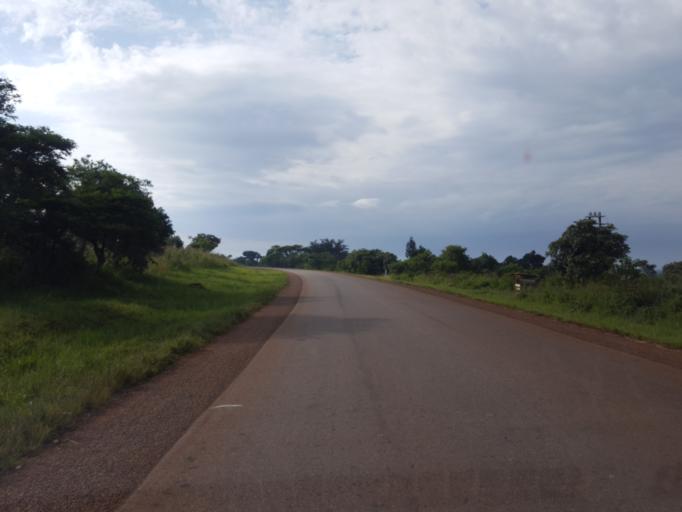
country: UG
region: Western Region
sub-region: Hoima District
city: Hoima
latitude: 1.2561
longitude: 31.5122
